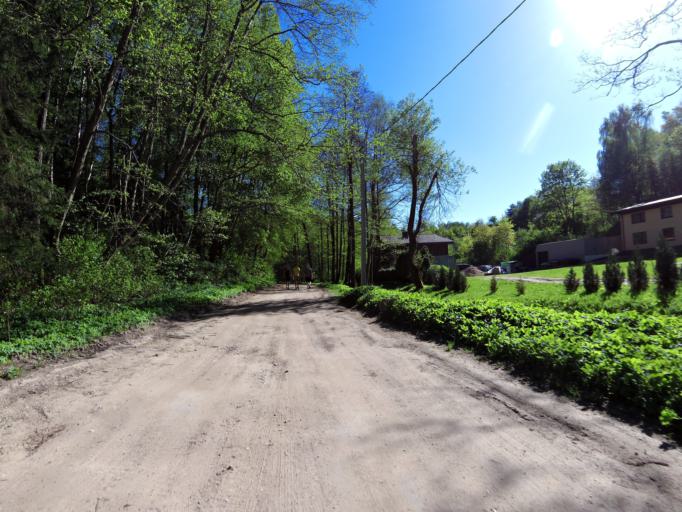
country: LT
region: Vilnius County
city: Pilaite
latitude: 54.6880
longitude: 25.1557
